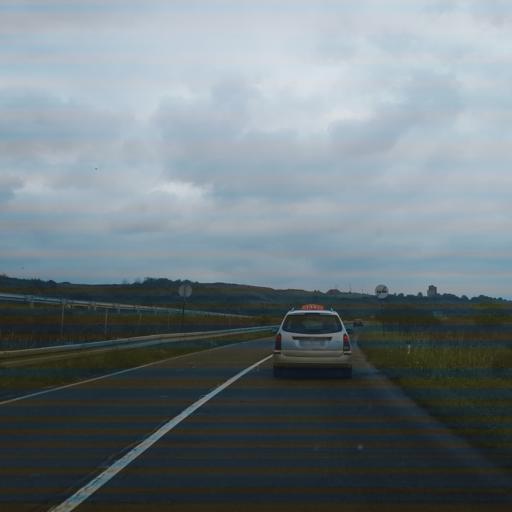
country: RS
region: Central Serbia
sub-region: Nisavski Okrug
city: Aleksinac
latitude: 43.5709
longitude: 21.6740
